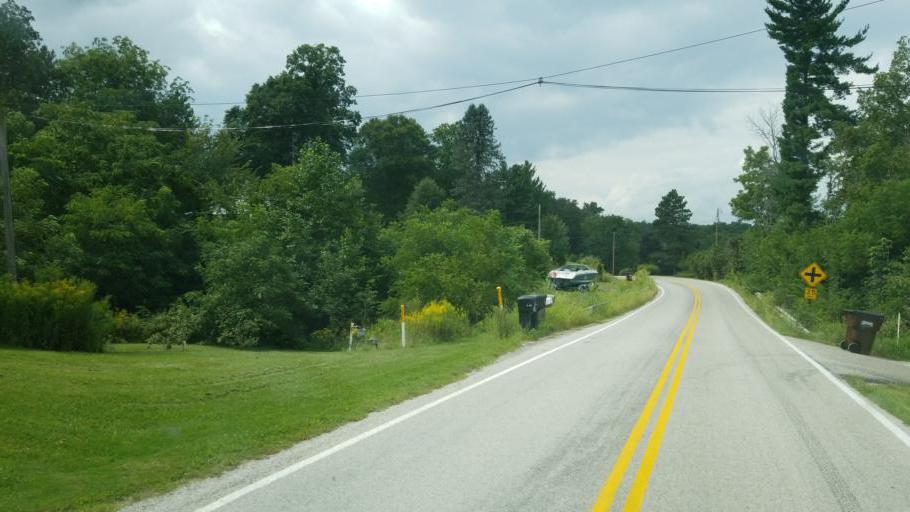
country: US
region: Ohio
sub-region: Ashland County
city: Loudonville
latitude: 40.6319
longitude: -82.3652
